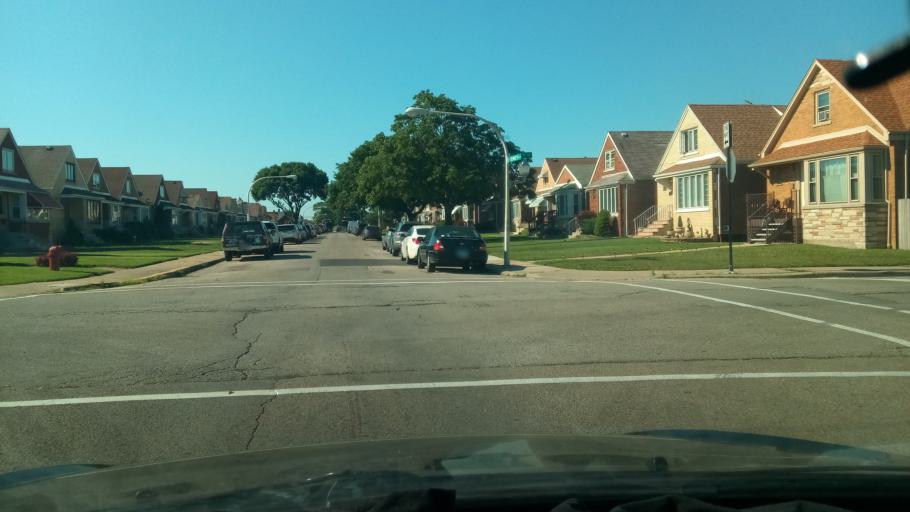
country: US
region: Illinois
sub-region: Cook County
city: Hometown
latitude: 41.7734
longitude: -87.7336
